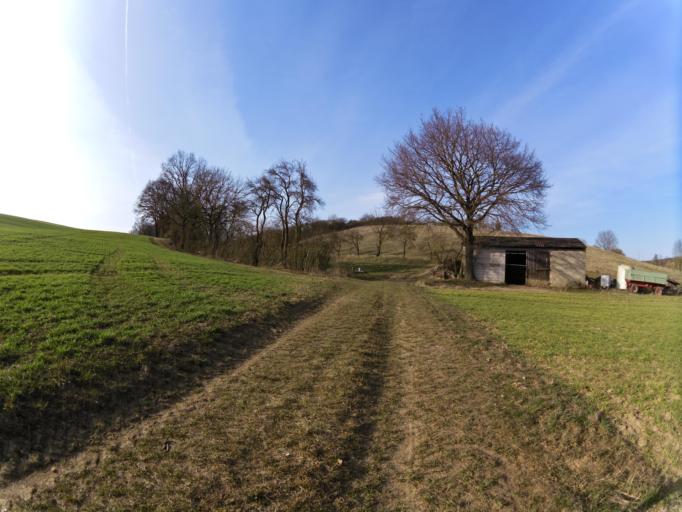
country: DE
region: Bavaria
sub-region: Regierungsbezirk Unterfranken
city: Dettelbach
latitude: 49.8226
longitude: 10.1474
